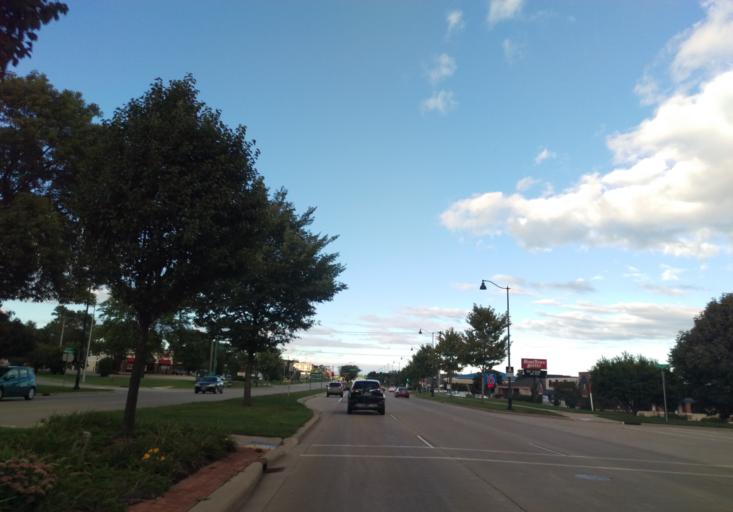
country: US
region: Wisconsin
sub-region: Dane County
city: Monona
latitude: 43.1225
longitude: -89.3162
